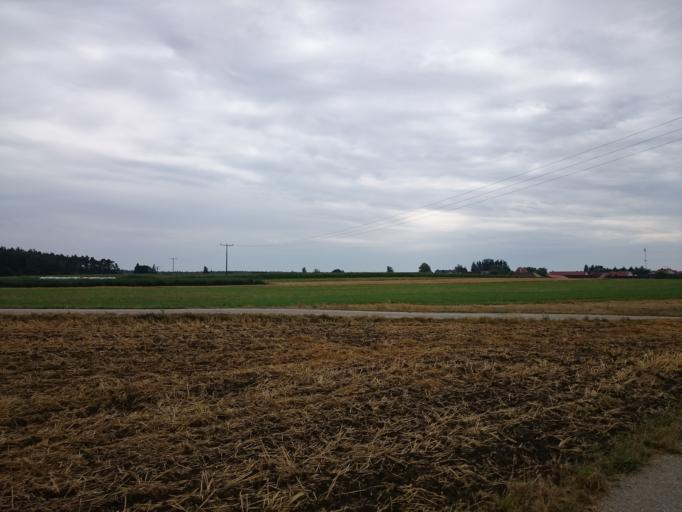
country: DE
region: Bavaria
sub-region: Regierungsbezirk Mittelfranken
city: Wendelstein
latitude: 49.3277
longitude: 11.1264
